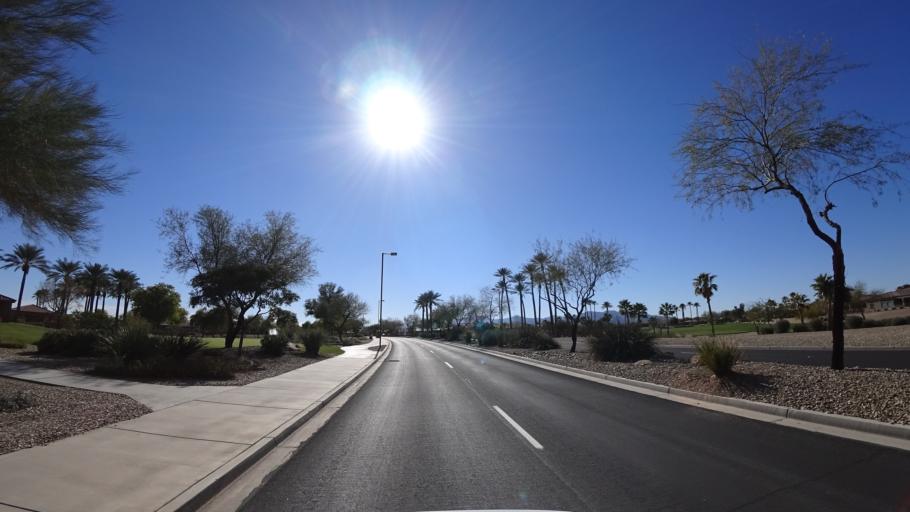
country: US
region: Arizona
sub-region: Maricopa County
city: Sun City West
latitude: 33.6650
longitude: -112.4271
